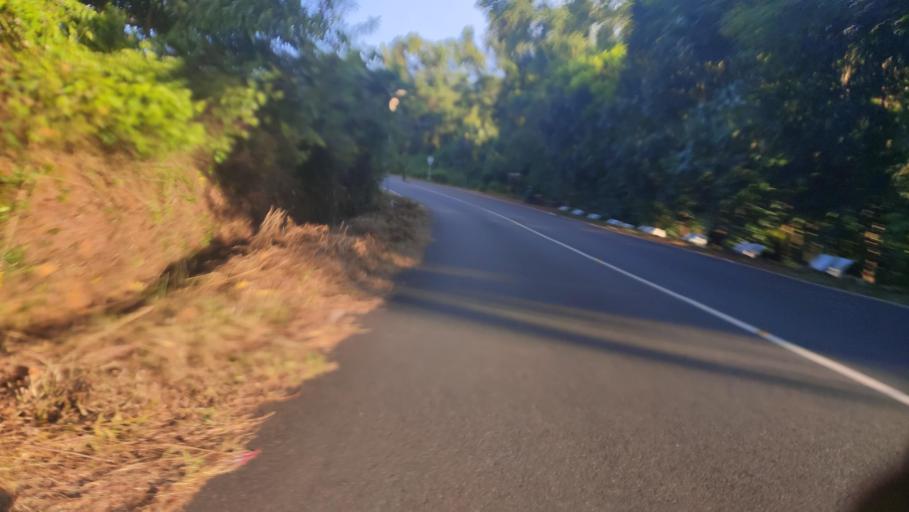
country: IN
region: Kerala
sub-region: Kasaragod District
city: Kasaragod
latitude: 12.4578
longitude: 75.0888
